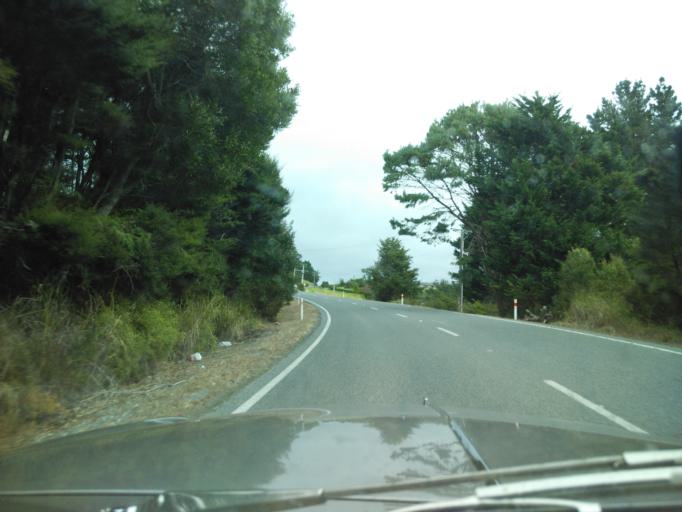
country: NZ
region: Auckland
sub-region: Auckland
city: Wellsford
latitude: -36.1320
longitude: 174.5451
